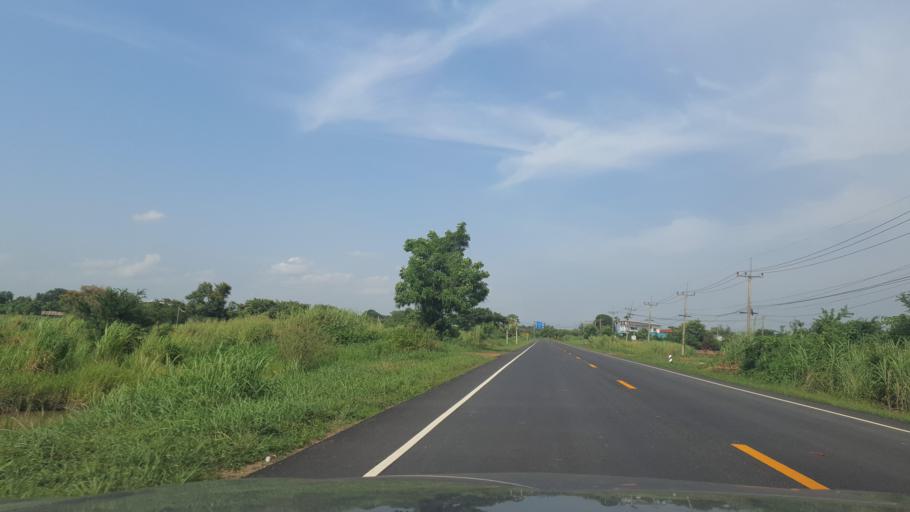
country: TH
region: Sukhothai
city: Si Samrong
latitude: 17.1716
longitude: 99.8462
